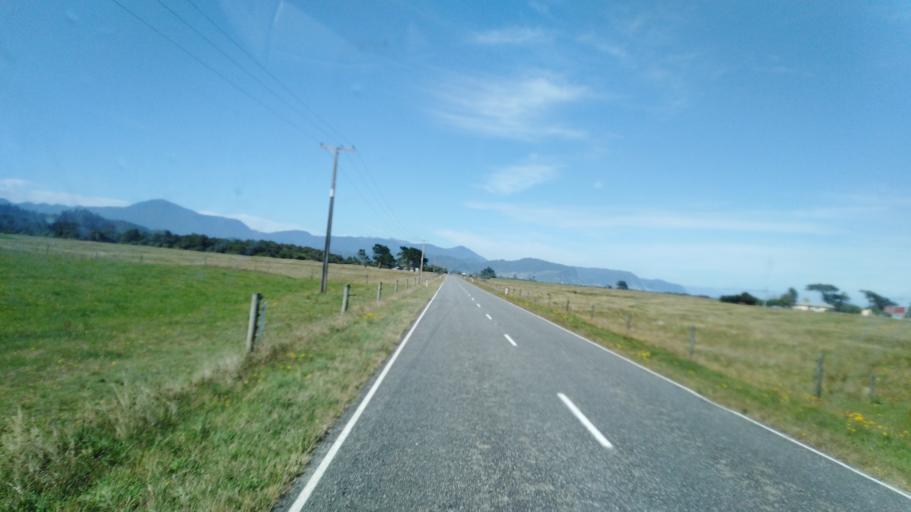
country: NZ
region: West Coast
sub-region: Buller District
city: Westport
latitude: -41.3099
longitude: 172.0911
